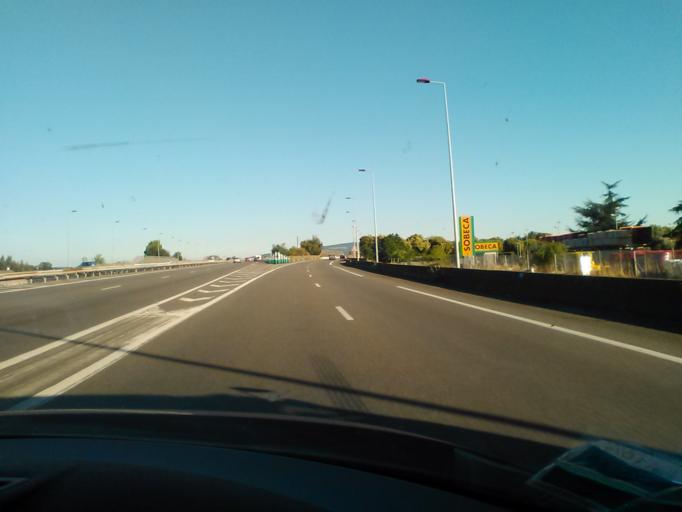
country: FR
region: Rhone-Alpes
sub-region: Departement du Rhone
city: Anse
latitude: 45.9400
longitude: 4.7227
